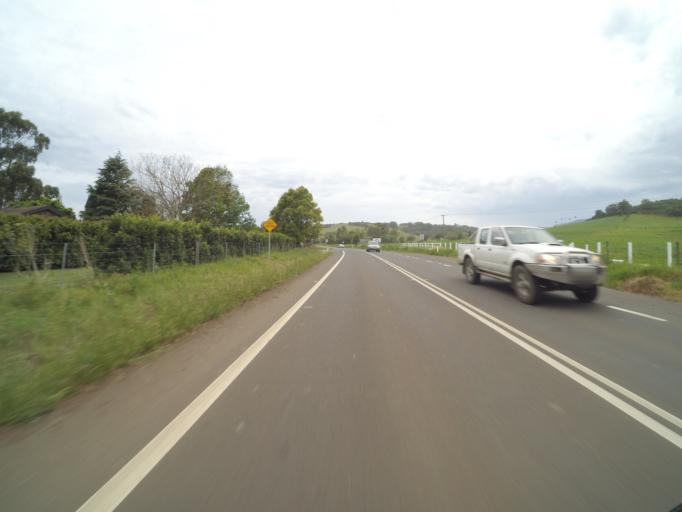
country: AU
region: New South Wales
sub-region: Kiama
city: Jamberoo
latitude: -34.6495
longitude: 150.7910
